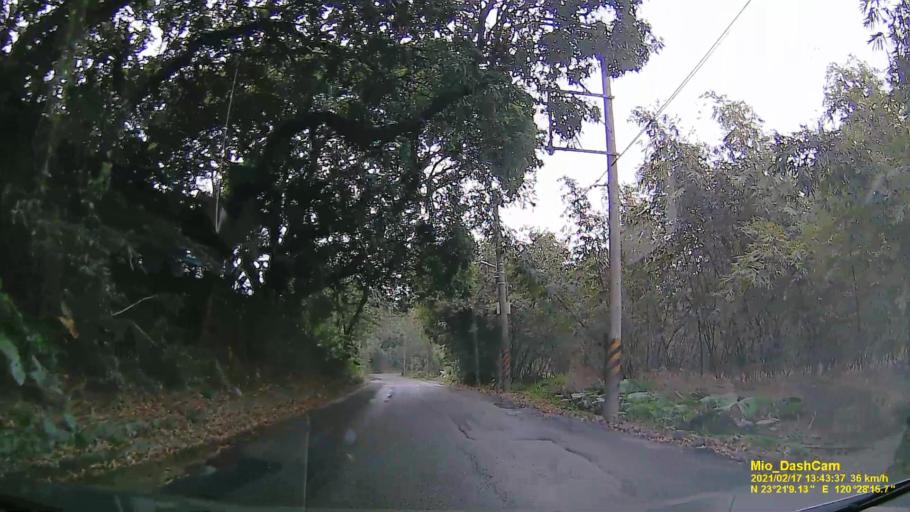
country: TW
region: Taiwan
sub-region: Chiayi
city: Jiayi Shi
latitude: 23.3525
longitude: 120.4710
